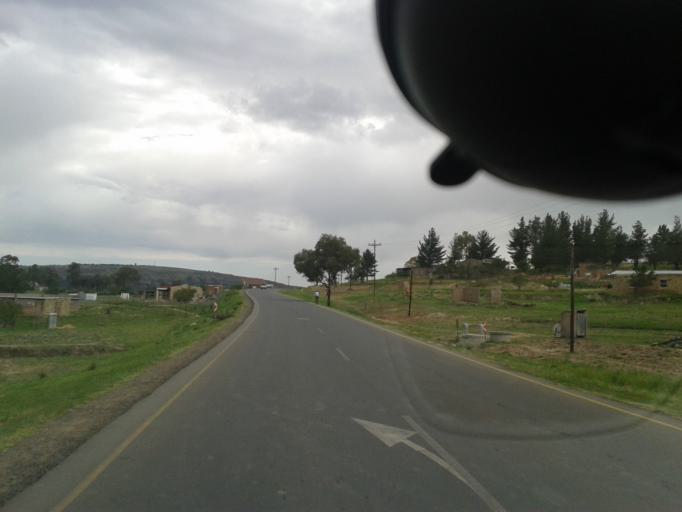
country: LS
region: Maseru
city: Maseru
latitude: -29.3545
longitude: 27.6540
